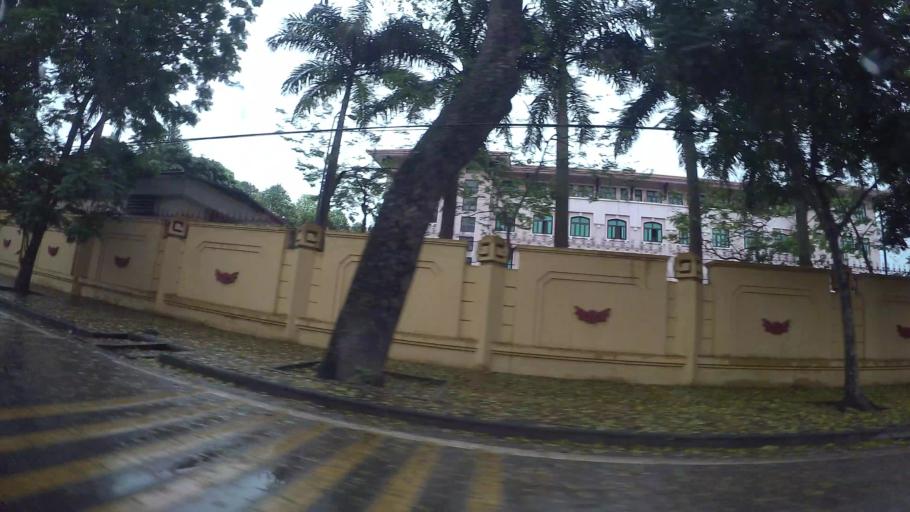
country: VN
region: Ha Noi
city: Hoan Kiem
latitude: 21.0382
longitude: 105.8416
